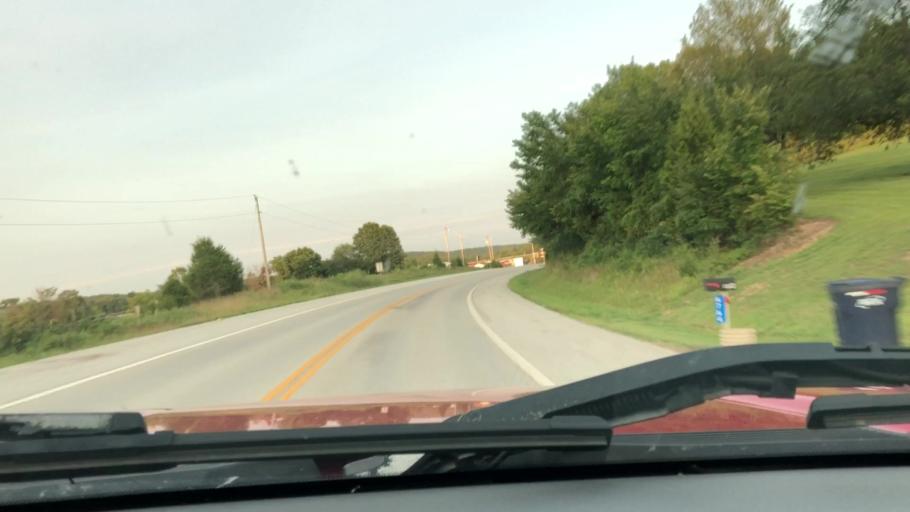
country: US
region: Missouri
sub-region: Jasper County
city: Duquesne
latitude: 36.9696
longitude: -94.4370
